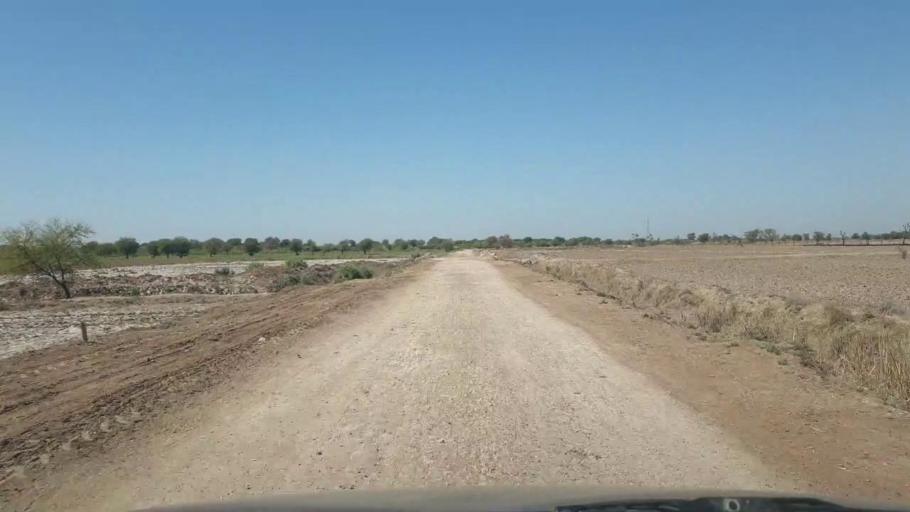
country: PK
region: Sindh
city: Dhoro Naro
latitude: 25.4503
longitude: 69.6120
